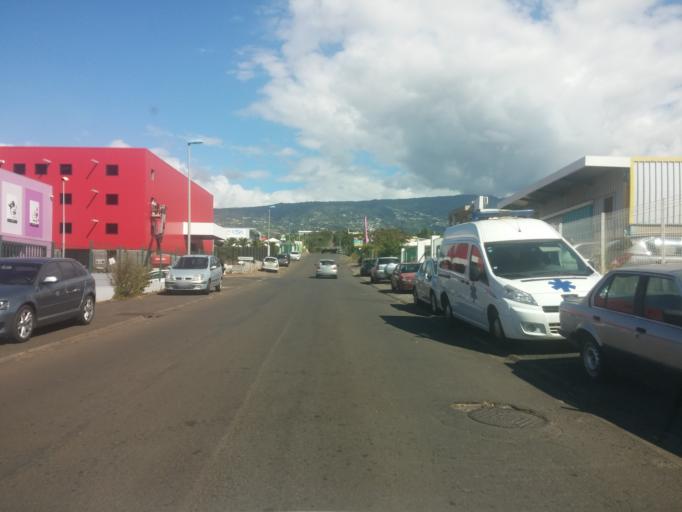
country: RE
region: Reunion
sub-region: Reunion
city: Sainte-Marie
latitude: -20.8992
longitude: 55.5336
